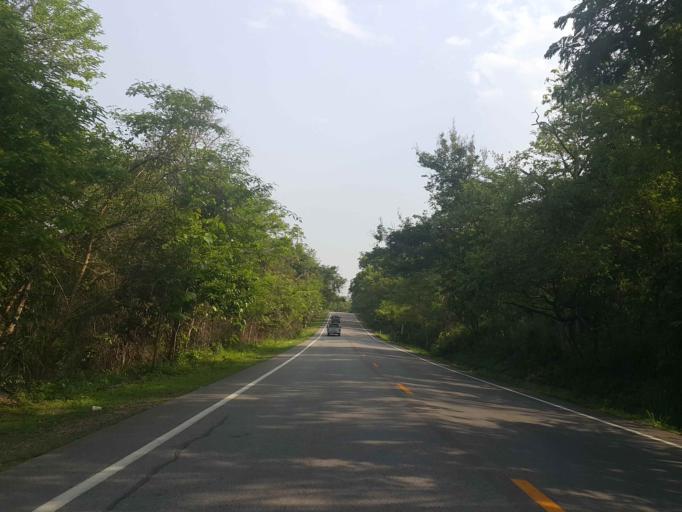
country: TH
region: Chiang Mai
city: Mae Taeng
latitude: 19.0786
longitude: 98.9792
